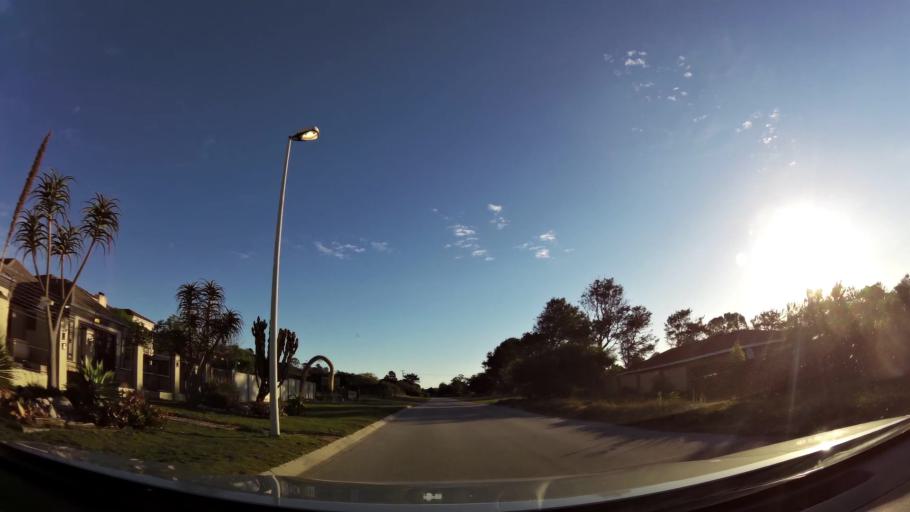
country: ZA
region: Eastern Cape
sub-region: Nelson Mandela Bay Metropolitan Municipality
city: Port Elizabeth
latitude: -33.9852
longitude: 25.4951
